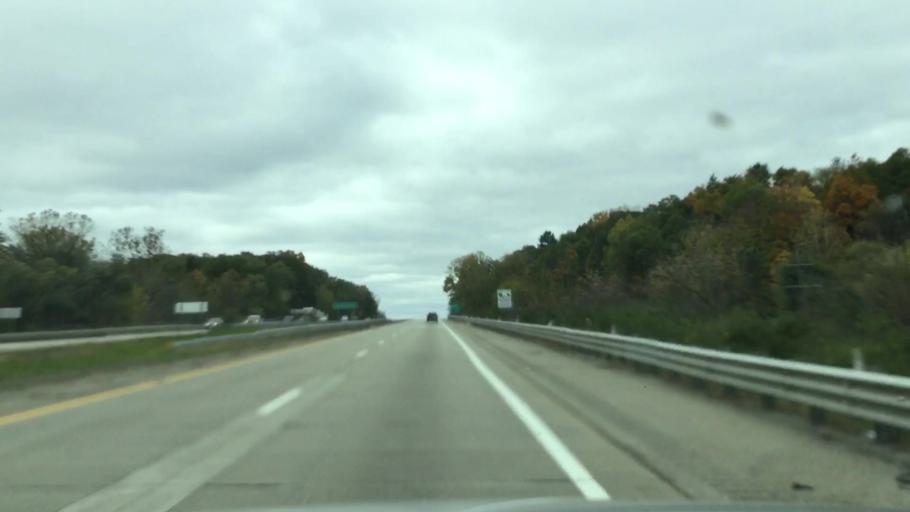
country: US
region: Michigan
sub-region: Washtenaw County
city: Ann Arbor
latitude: 42.2983
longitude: -83.7538
